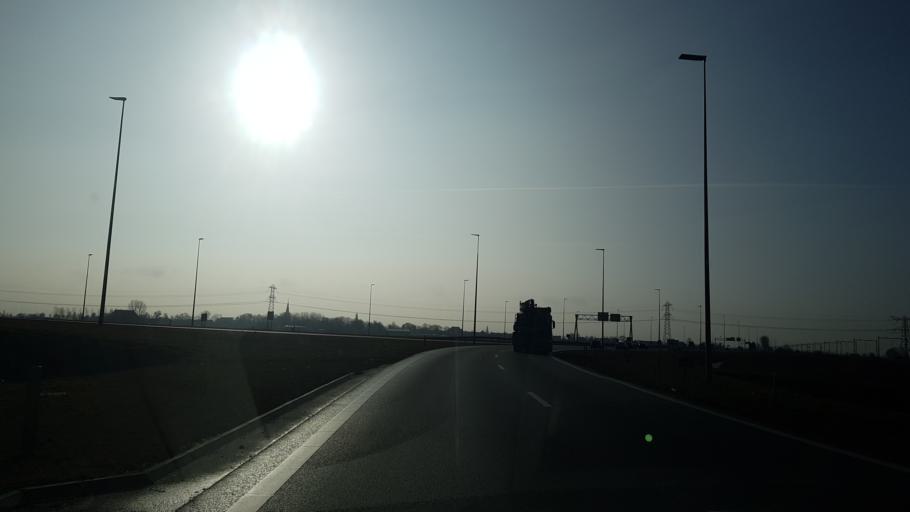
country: NL
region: Friesland
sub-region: Gemeente Leeuwarden
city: Wirdum
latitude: 53.1565
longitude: 5.7898
